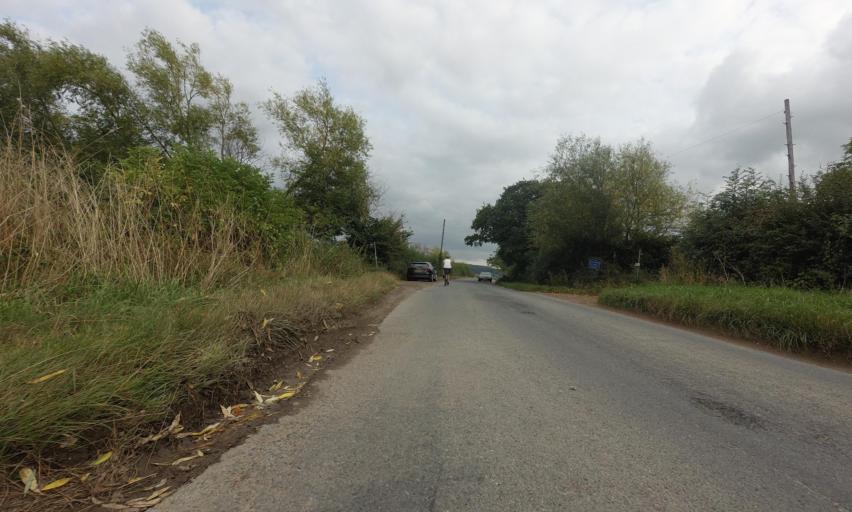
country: GB
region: England
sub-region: Gloucestershire
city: Winchcombe
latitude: 51.9717
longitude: -1.9757
